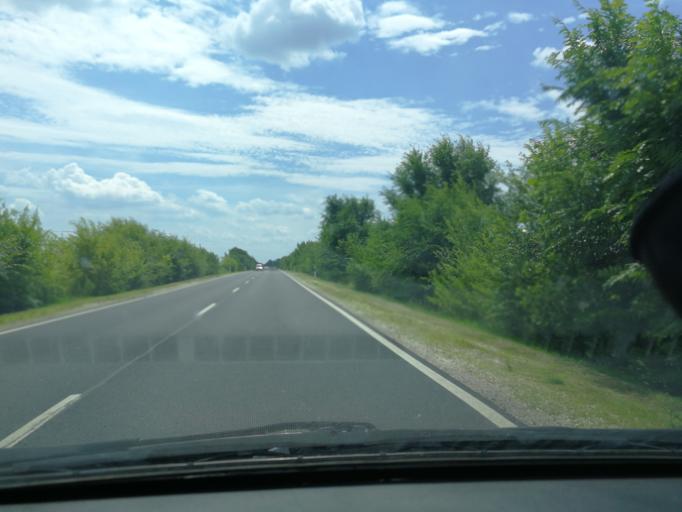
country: HU
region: Bacs-Kiskun
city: Dunapataj
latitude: 46.6170
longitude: 18.9905
